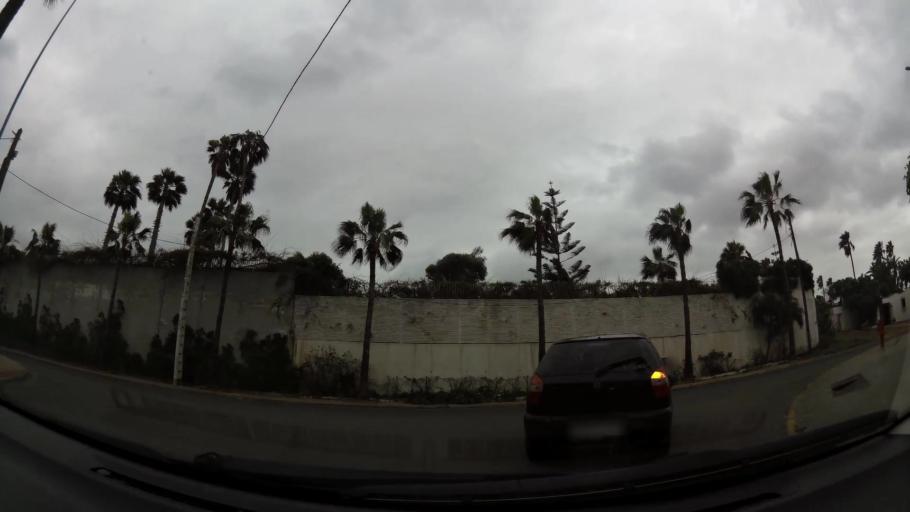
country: MA
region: Grand Casablanca
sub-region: Casablanca
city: Casablanca
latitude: 33.5998
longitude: -7.6603
